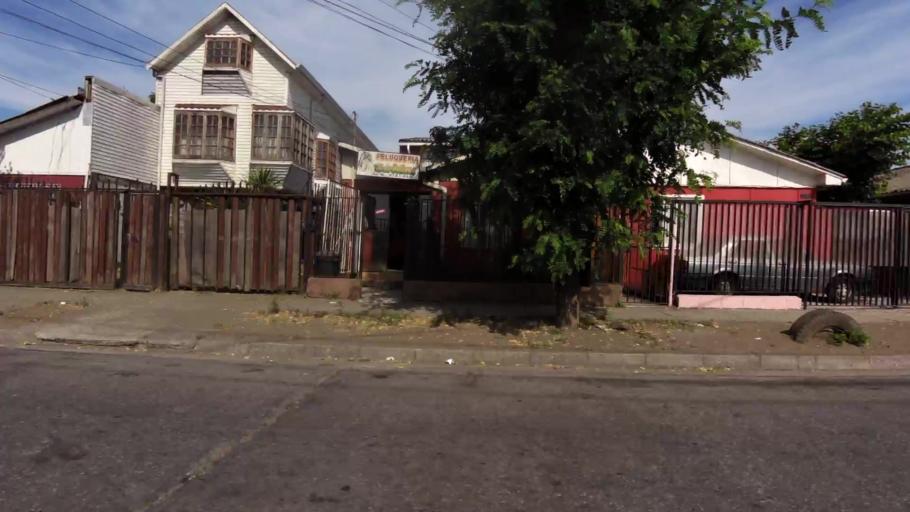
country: CL
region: Biobio
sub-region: Provincia de Concepcion
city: Talcahuano
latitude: -36.7859
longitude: -73.1017
